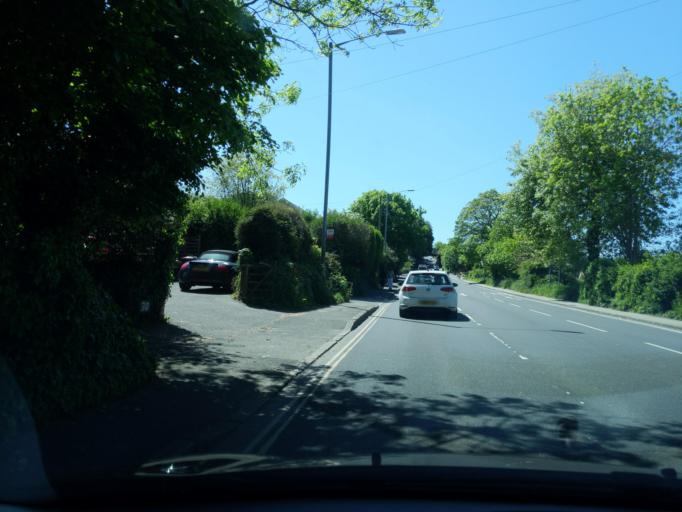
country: GB
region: England
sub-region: Cornwall
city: St Austell
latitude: 50.3389
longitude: -4.7625
